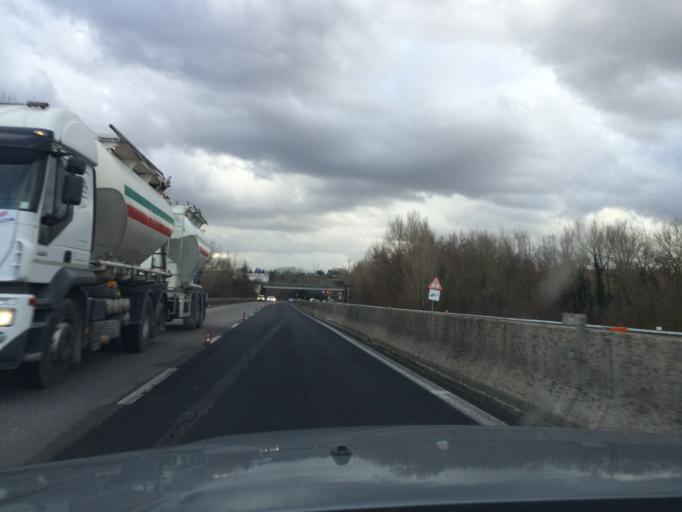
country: IT
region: Umbria
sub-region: Provincia di Terni
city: San Gemini
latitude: 42.6394
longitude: 12.5430
